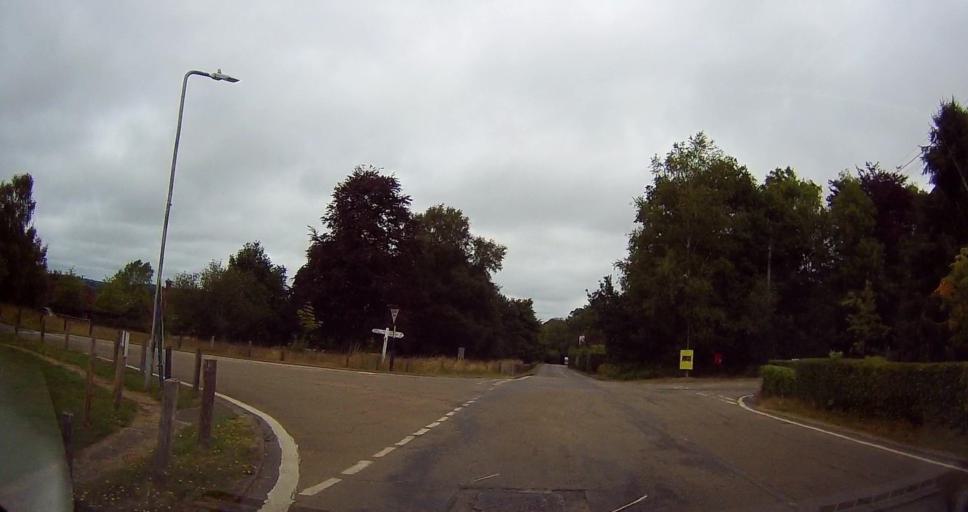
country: GB
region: England
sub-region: East Sussex
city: Wadhurst
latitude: 51.0945
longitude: 0.3877
